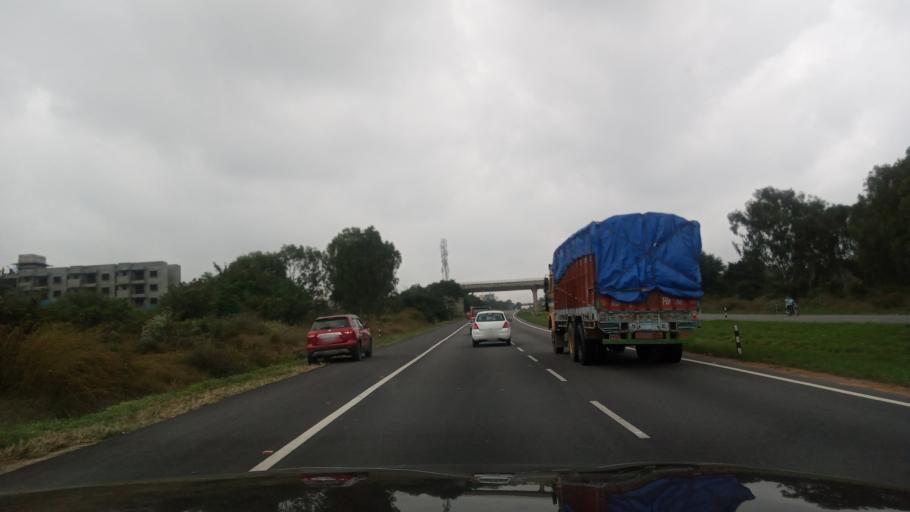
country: IN
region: Karnataka
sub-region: Bangalore Urban
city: Bangalore
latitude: 12.8655
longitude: 77.6422
